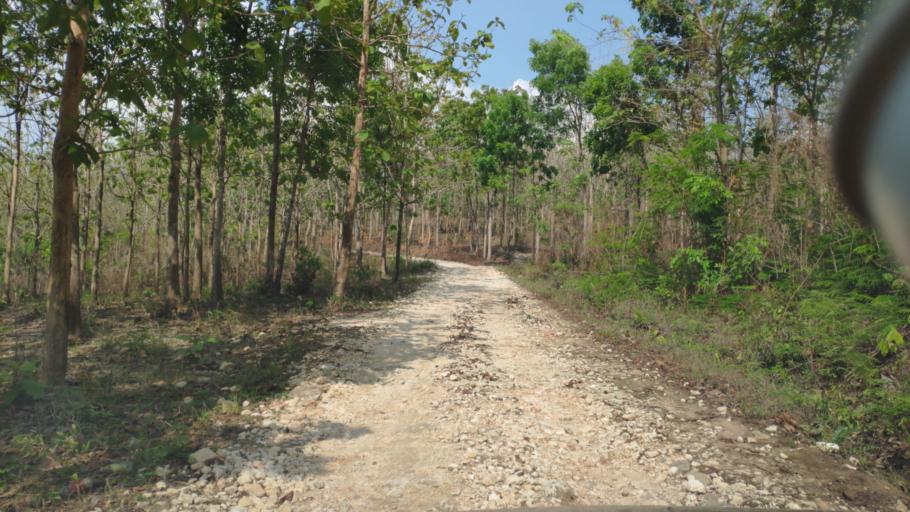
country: ID
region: Central Java
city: Semanggi
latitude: -7.0578
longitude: 111.4161
